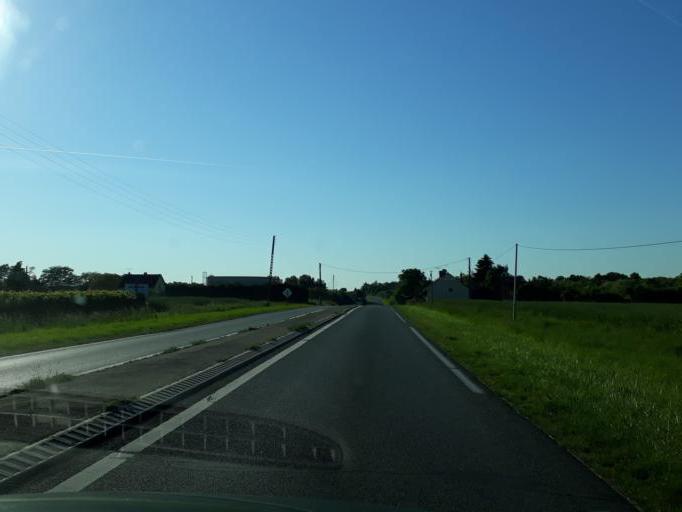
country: FR
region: Centre
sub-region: Departement du Loiret
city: Bonny-sur-Loire
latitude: 47.5904
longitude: 2.8034
